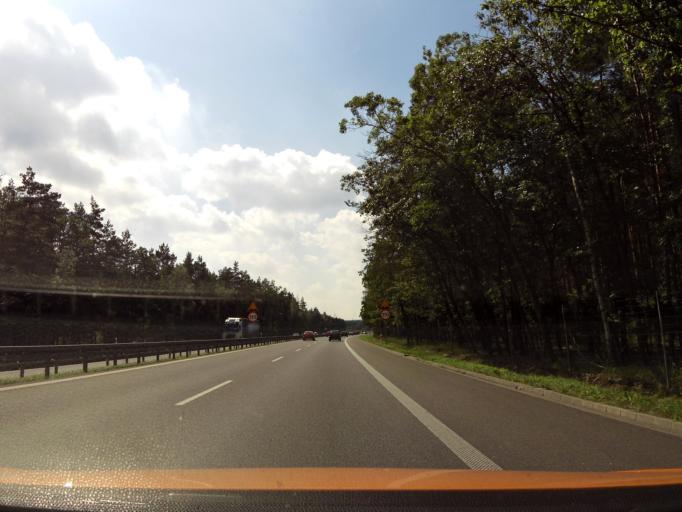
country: PL
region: West Pomeranian Voivodeship
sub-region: Powiat gryfinski
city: Stare Czarnowo
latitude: 53.3826
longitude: 14.7113
